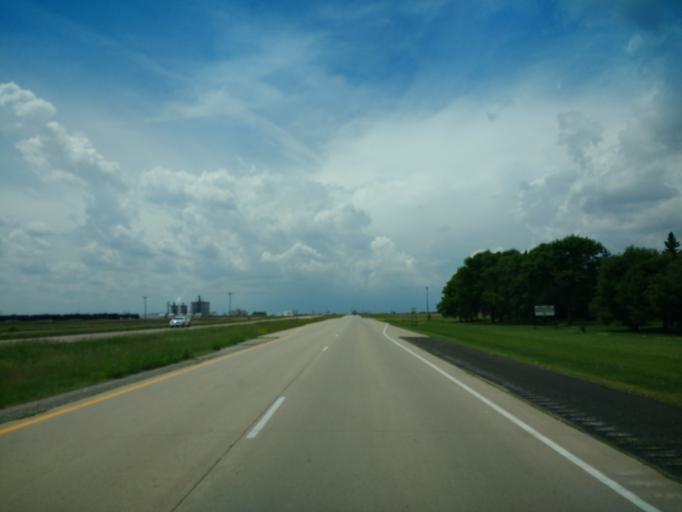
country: US
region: Minnesota
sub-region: Cottonwood County
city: Windom
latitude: 43.8132
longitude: -95.2734
